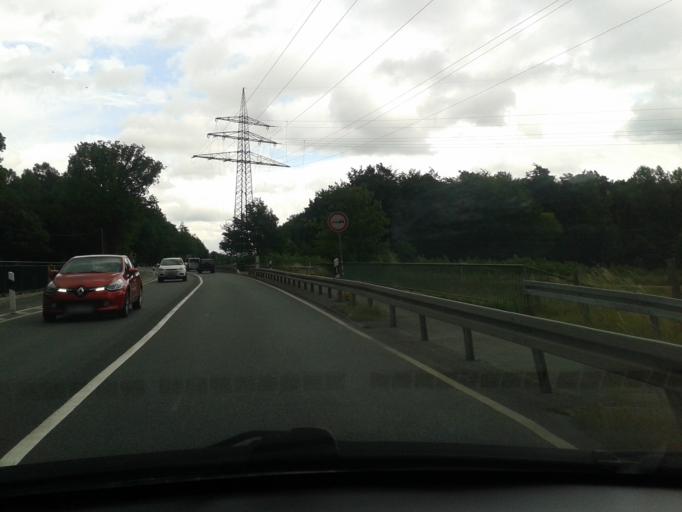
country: DE
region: North Rhine-Westphalia
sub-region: Regierungsbezirk Detmold
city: Paderborn
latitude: 51.7571
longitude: 8.7682
